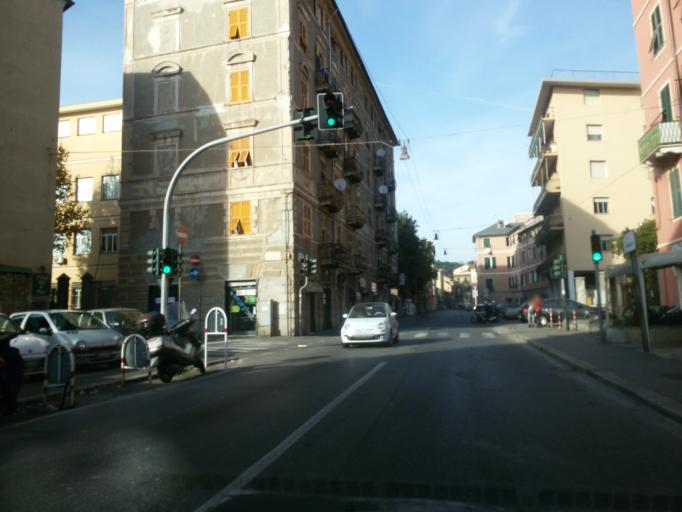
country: IT
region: Liguria
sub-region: Provincia di Genova
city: Genoa
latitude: 44.4482
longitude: 8.8941
